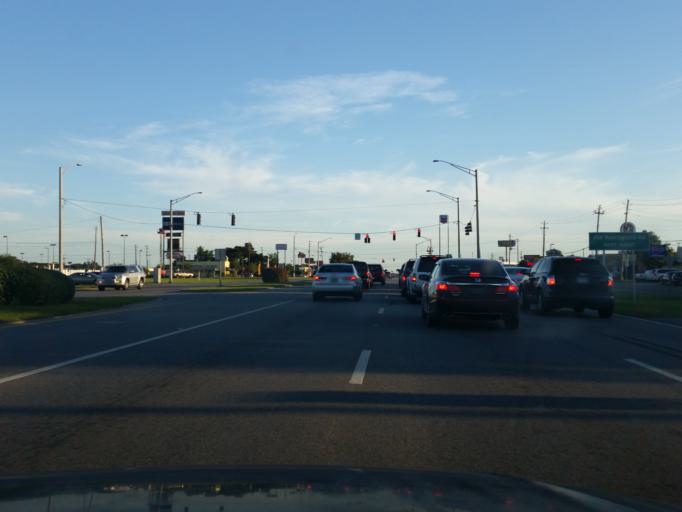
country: US
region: Alabama
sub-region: Mobile County
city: Tillmans Corner
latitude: 30.5923
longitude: -88.1693
